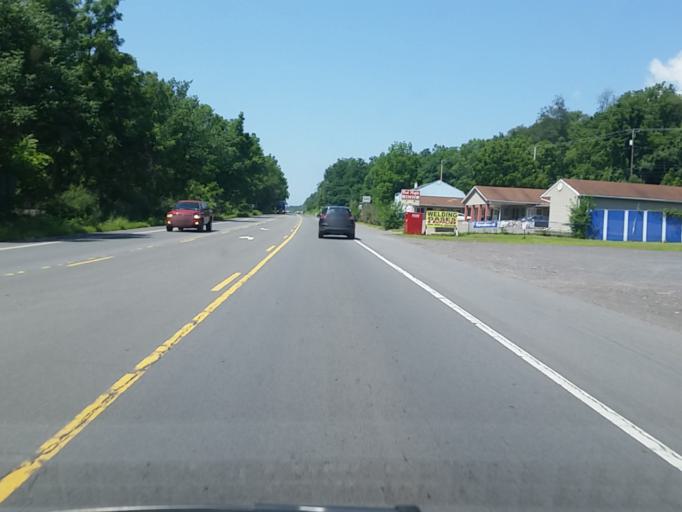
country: US
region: Pennsylvania
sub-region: Columbia County
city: Mifflinville
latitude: 41.0458
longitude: -76.2906
